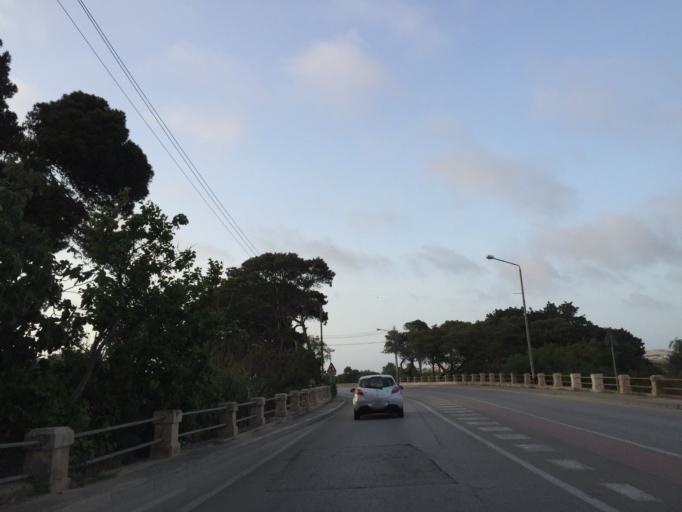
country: MT
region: Il-Mosta
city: Mosta
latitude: 35.9237
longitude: 14.4156
